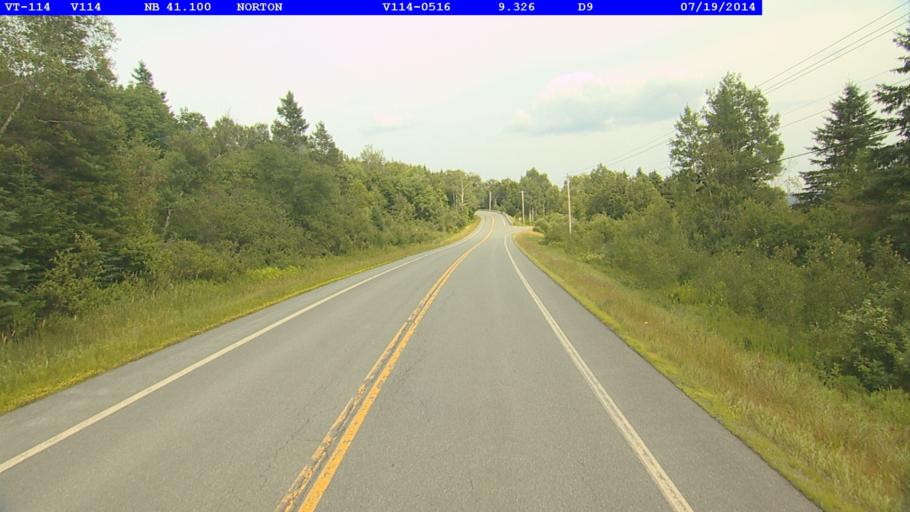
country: CA
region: Quebec
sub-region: Estrie
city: Coaticook
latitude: 44.9959
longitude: -71.7192
